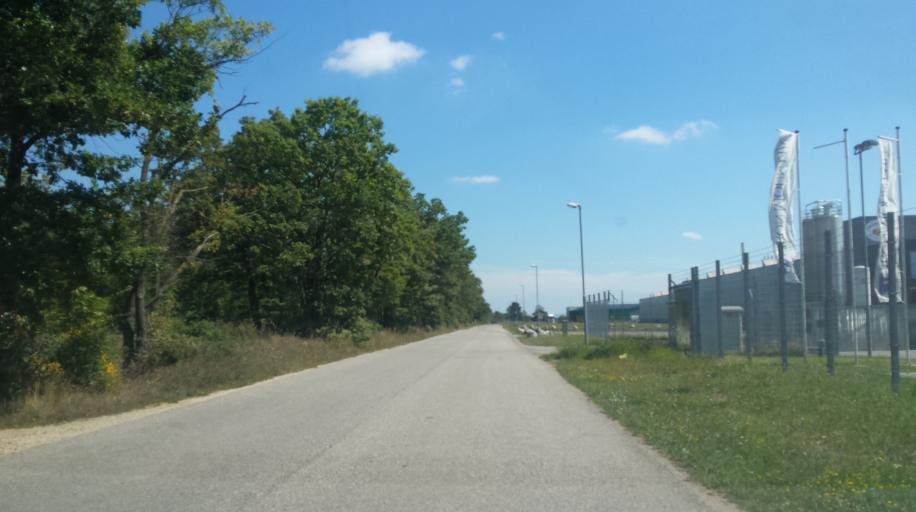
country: AT
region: Lower Austria
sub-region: Politischer Bezirk Ganserndorf
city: Parbasdorf
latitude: 48.3065
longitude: 16.6218
